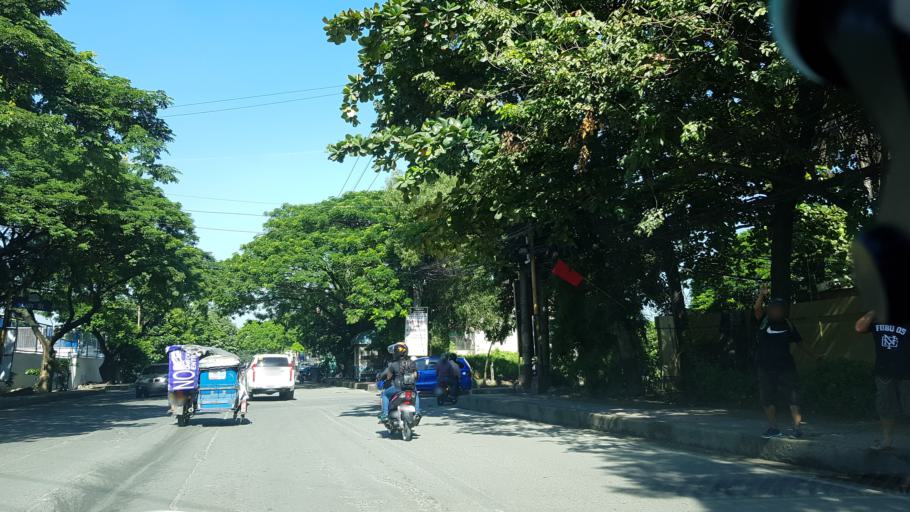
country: PH
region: Calabarzon
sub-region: Province of Rizal
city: Cainta
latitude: 14.5673
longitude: 121.0918
